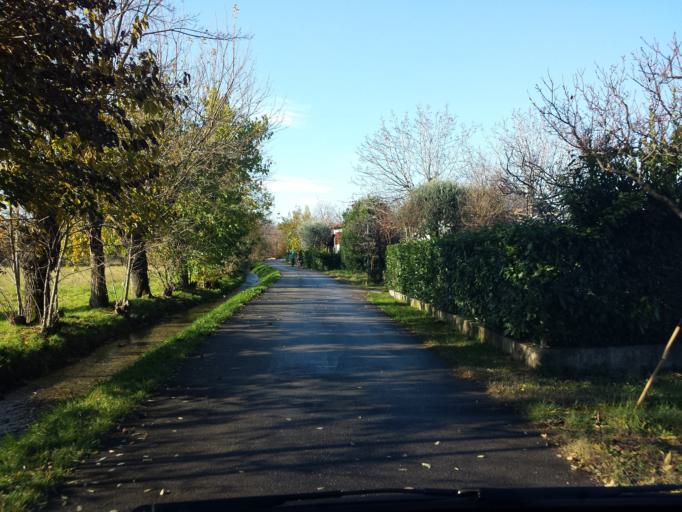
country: IT
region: Veneto
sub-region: Provincia di Vicenza
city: Sandrigo
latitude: 45.6820
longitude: 11.5877
